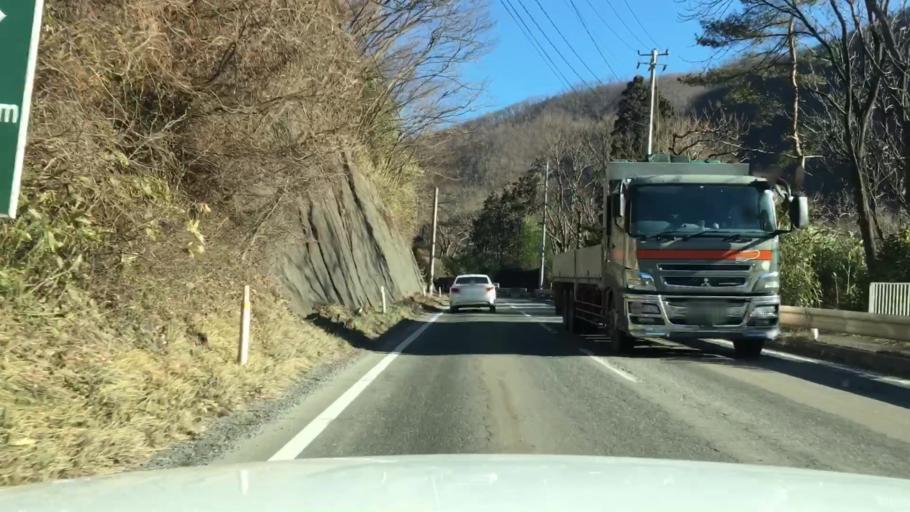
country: JP
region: Iwate
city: Miyako
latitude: 39.6198
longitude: 141.8096
